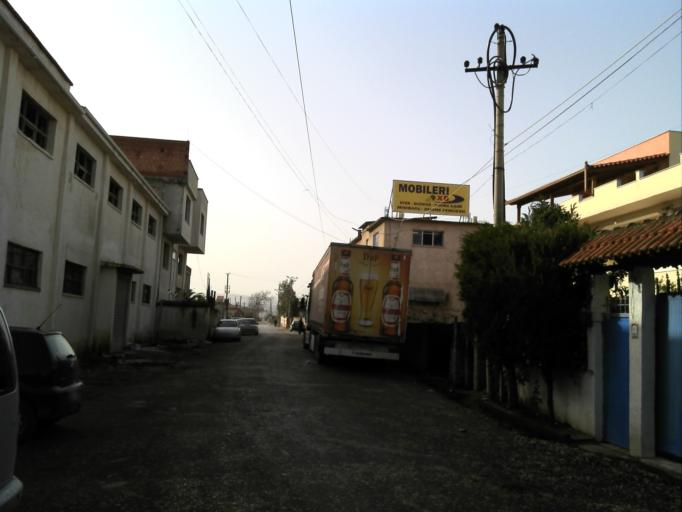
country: AL
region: Fier
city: Fier
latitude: 40.7279
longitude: 19.5482
